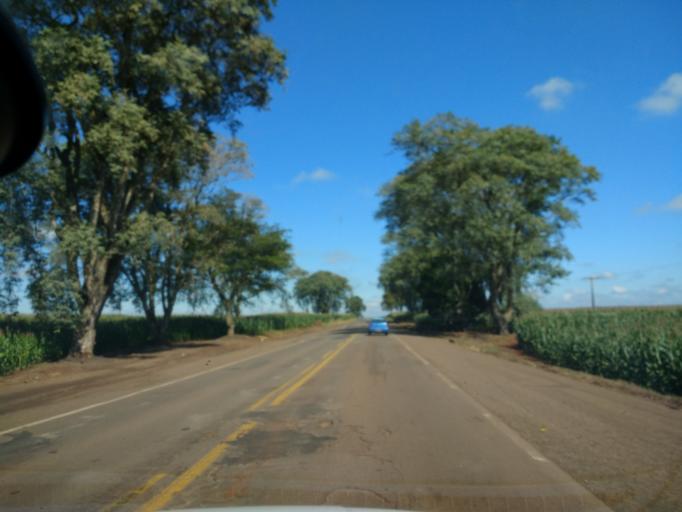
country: BR
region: Parana
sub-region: Terra Boa
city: Terra Boa
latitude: -23.6084
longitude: -52.4191
